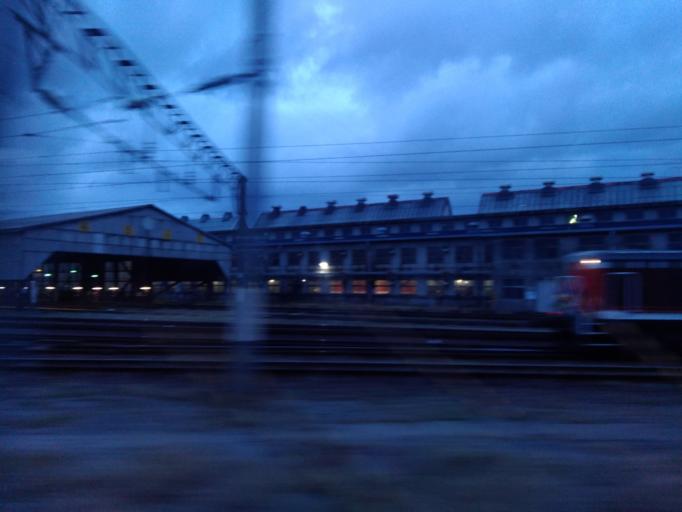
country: JP
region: Hokkaido
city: Hakodate
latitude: 41.7793
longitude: 140.7286
